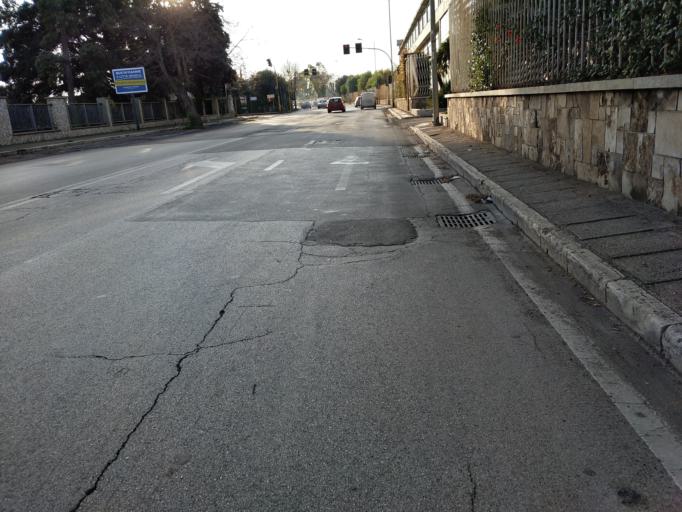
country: IT
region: Apulia
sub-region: Provincia di Bari
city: Bari
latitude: 41.1165
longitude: 16.8372
